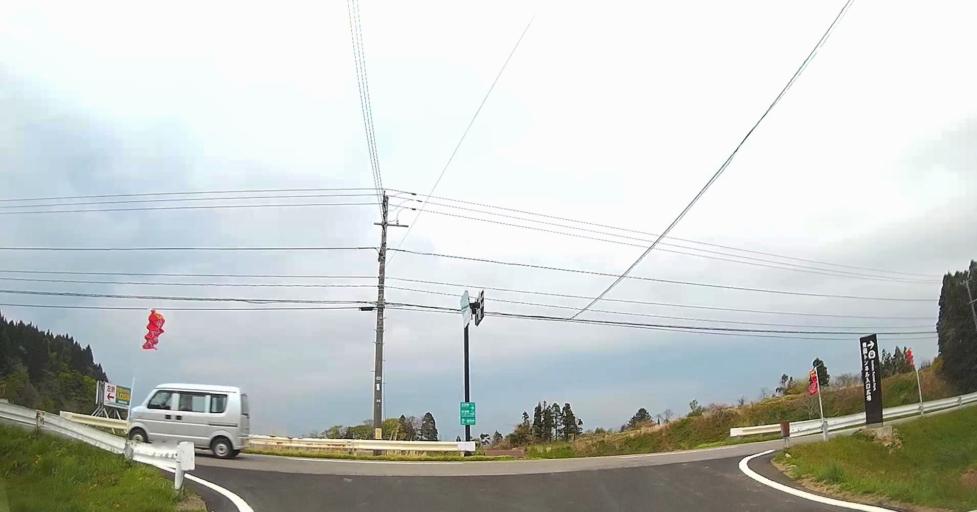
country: JP
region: Aomori
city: Shimokizukuri
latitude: 41.1805
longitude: 140.4603
